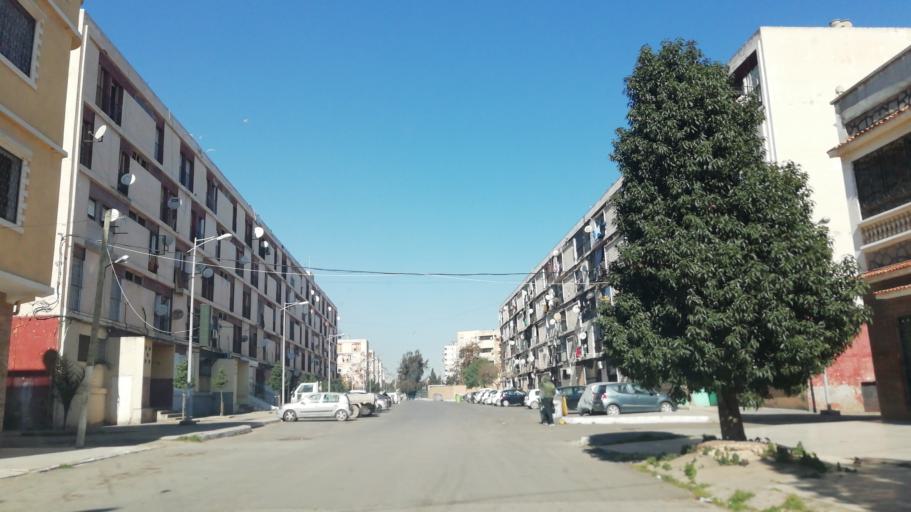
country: DZ
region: Oran
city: Oran
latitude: 35.6776
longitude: -0.6378
